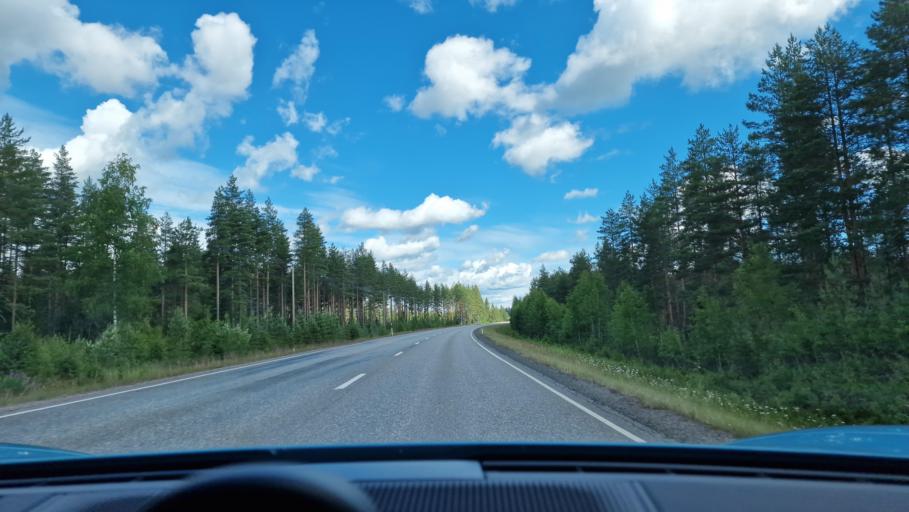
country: FI
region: Pirkanmaa
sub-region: Ylae-Pirkanmaa
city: Juupajoki
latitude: 61.7840
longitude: 24.3003
